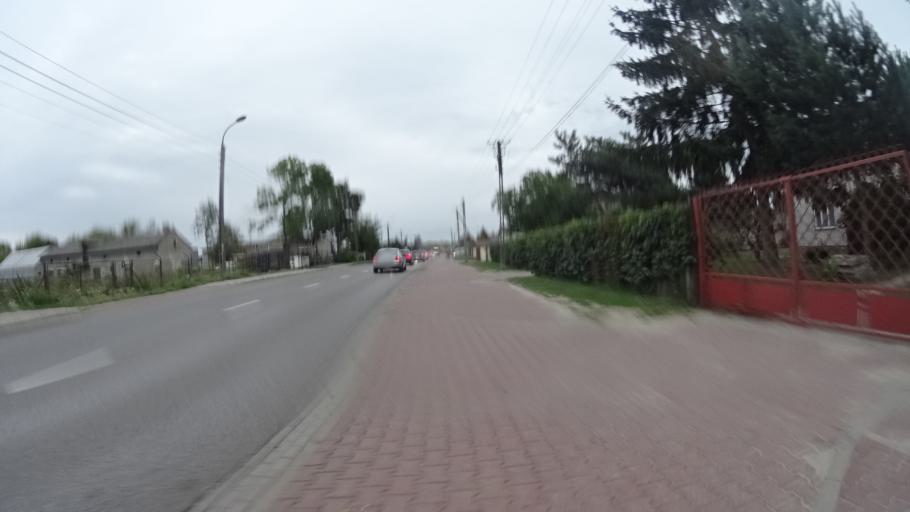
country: PL
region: Masovian Voivodeship
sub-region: Powiat warszawski zachodni
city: Stare Babice
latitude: 52.2535
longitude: 20.8022
